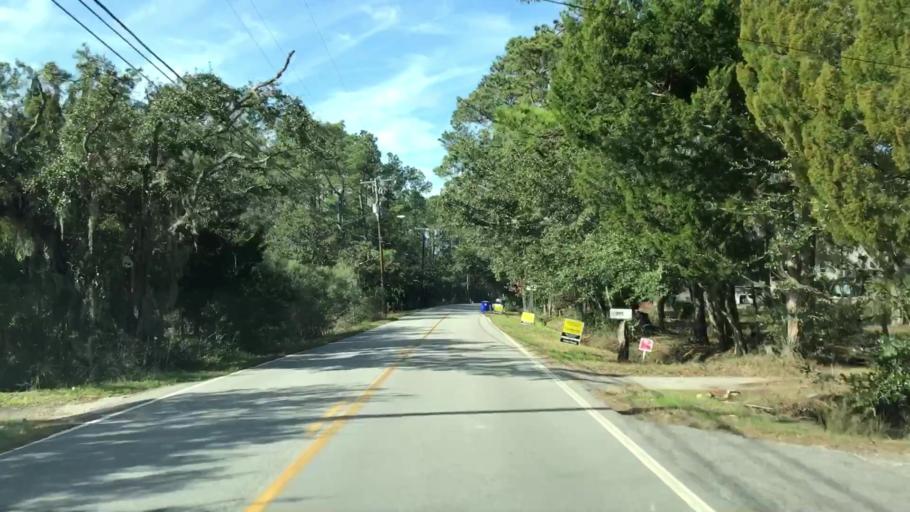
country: US
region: South Carolina
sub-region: Charleston County
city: Charleston
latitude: 32.7745
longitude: -80.0151
